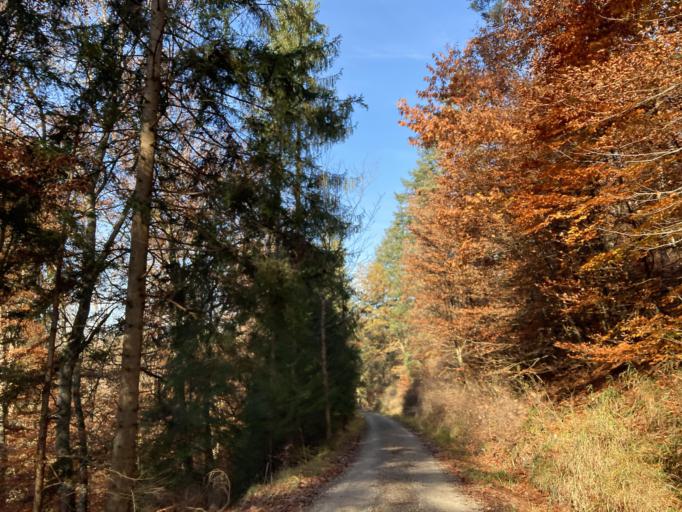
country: DE
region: Baden-Wuerttemberg
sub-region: Regierungsbezirk Stuttgart
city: Altdorf
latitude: 48.5801
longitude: 8.9986
